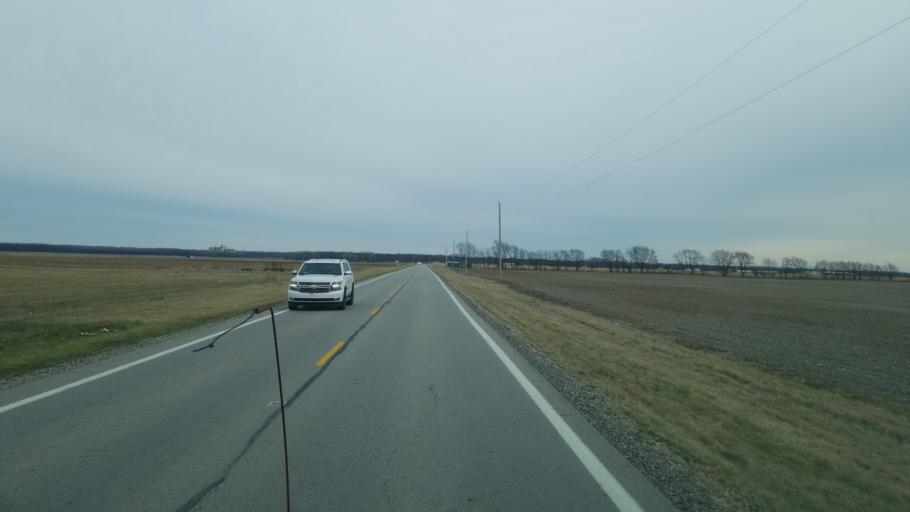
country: US
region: Ohio
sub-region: Pickaway County
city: Circleville
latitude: 39.6062
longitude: -82.9928
